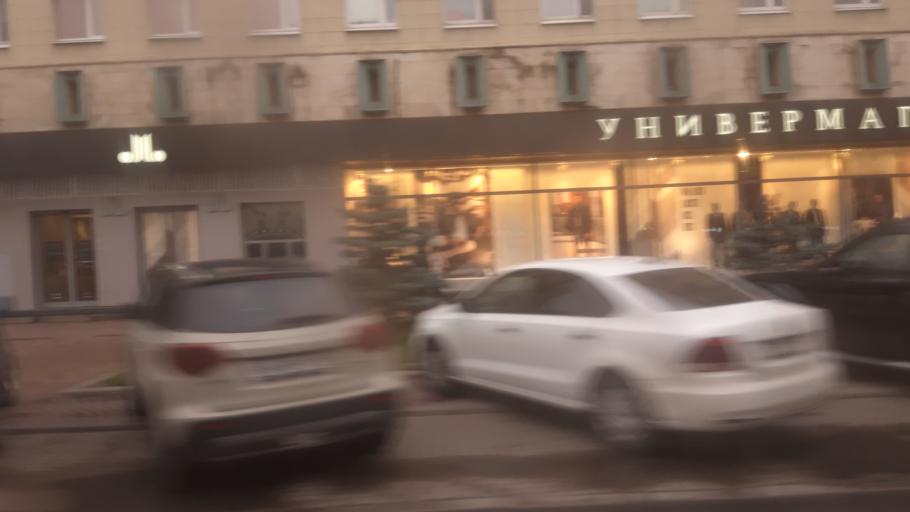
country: RU
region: St.-Petersburg
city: Kupchino
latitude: 59.8476
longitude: 30.3219
